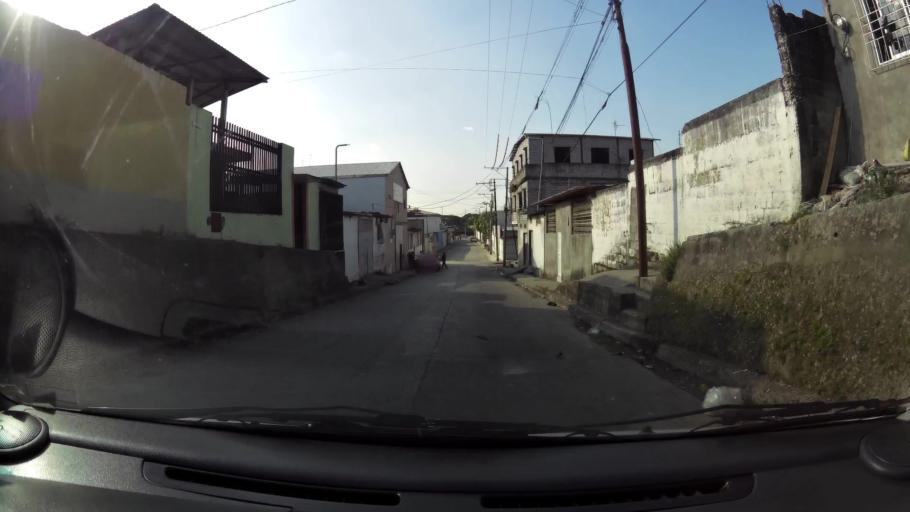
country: EC
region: Guayas
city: Guayaquil
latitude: -2.1422
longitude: -79.9302
